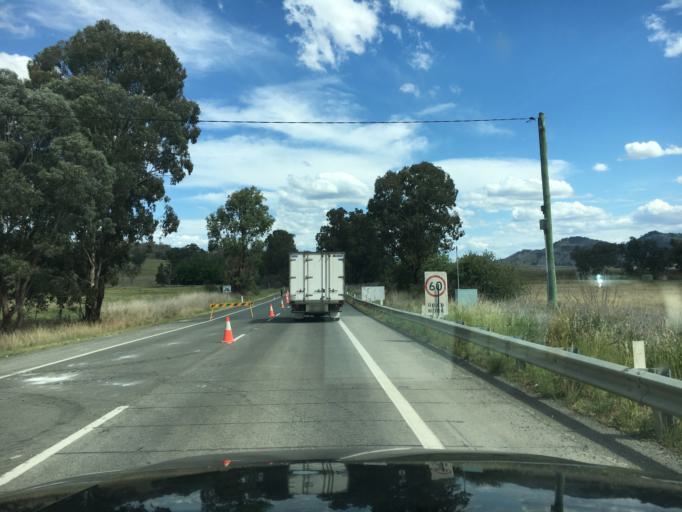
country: AU
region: New South Wales
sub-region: Liverpool Plains
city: Quirindi
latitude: -31.4593
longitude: 150.8606
